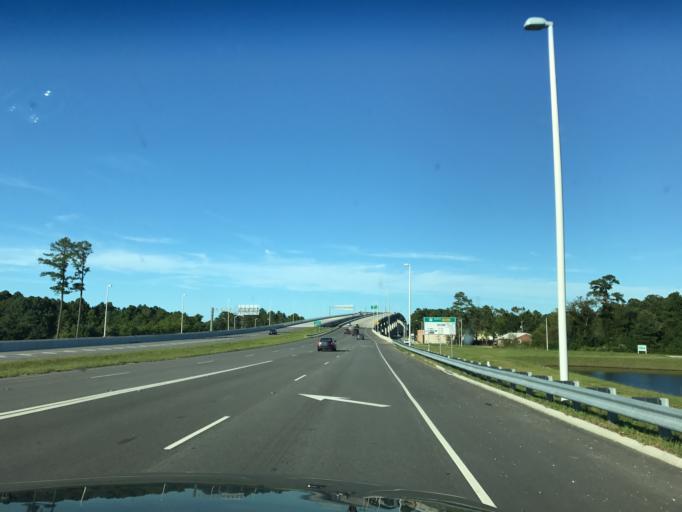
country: US
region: Virginia
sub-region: City of Chesapeake
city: Chesapeake
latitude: 36.7296
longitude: -76.3003
